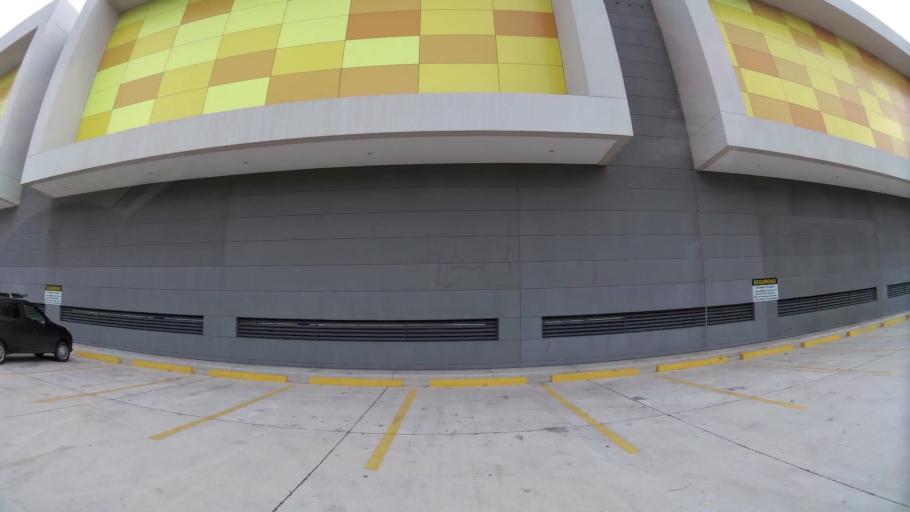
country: BO
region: Santa Cruz
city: Santa Cruz de la Sierra
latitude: -17.7767
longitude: -63.2147
